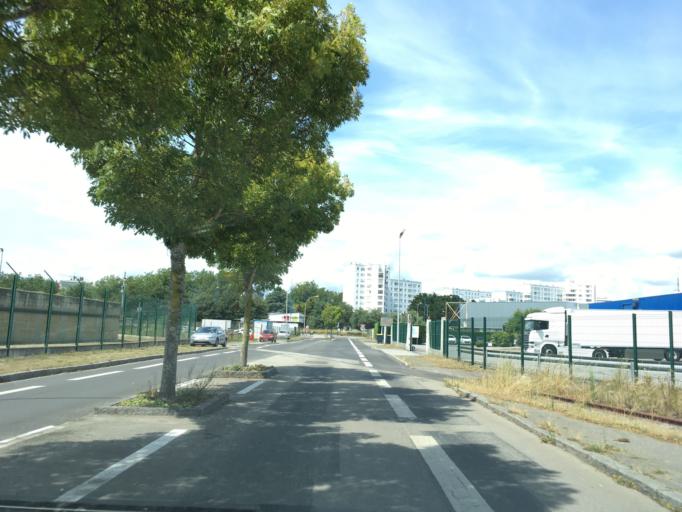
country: FR
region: Brittany
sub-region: Departement du Morbihan
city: Lorient
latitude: 47.7400
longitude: -3.3570
